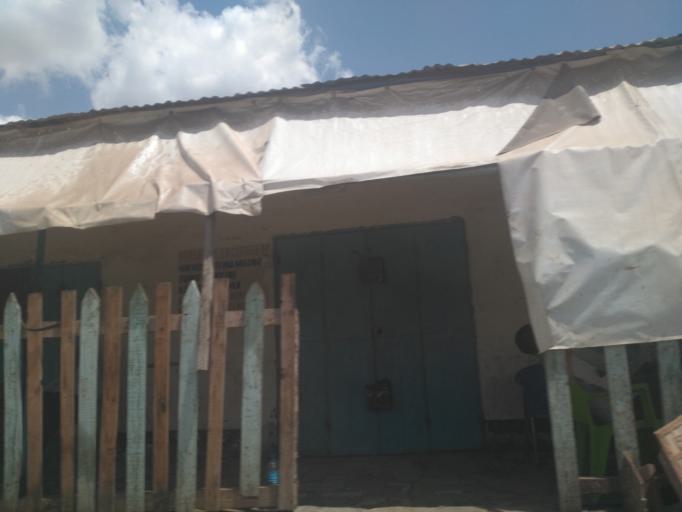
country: TZ
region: Dar es Salaam
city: Dar es Salaam
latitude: -6.8436
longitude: 39.2665
